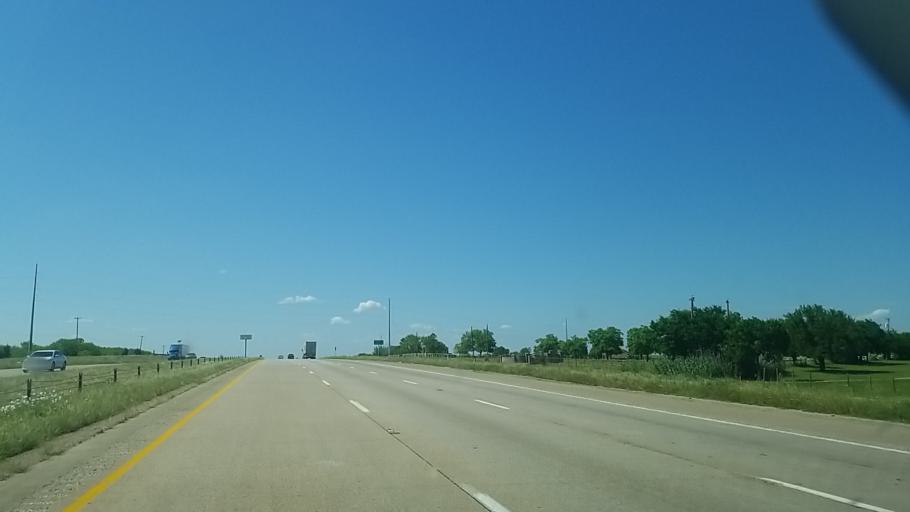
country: US
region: Texas
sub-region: Ellis County
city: Palmer
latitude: 32.3832
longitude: -96.6489
